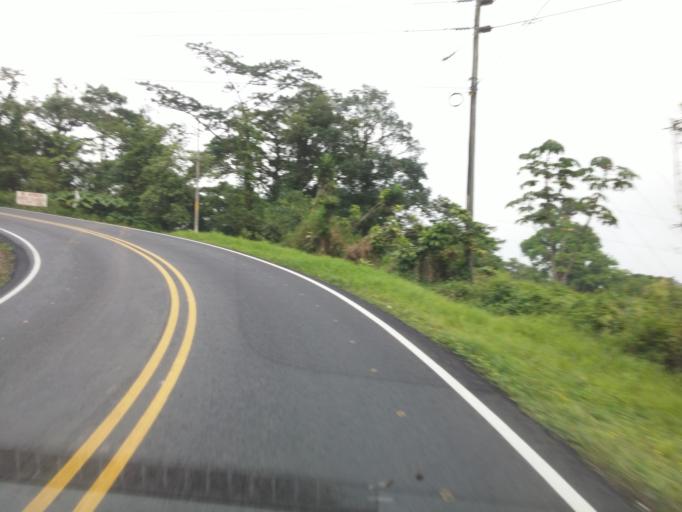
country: CR
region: Alajuela
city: San Ramon
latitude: 10.2025
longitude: -84.5235
